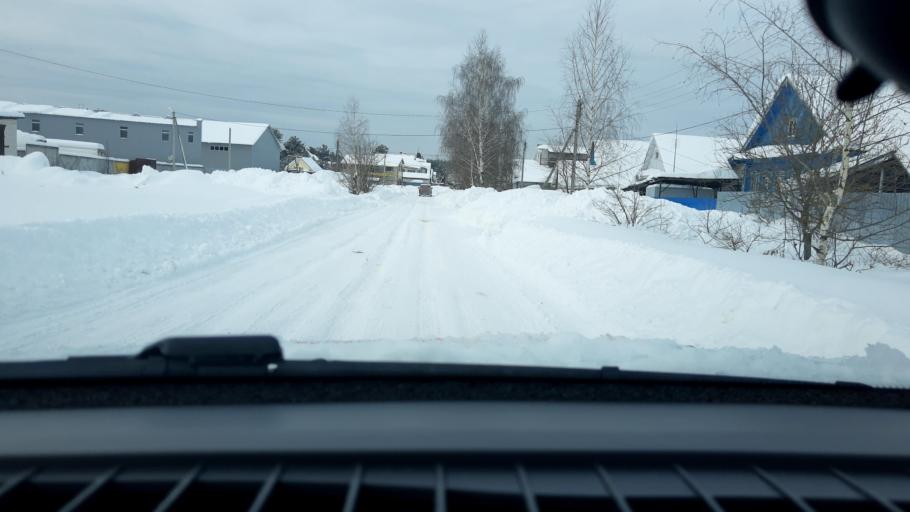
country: RU
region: Nizjnij Novgorod
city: Lukino
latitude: 56.3969
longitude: 43.6982
